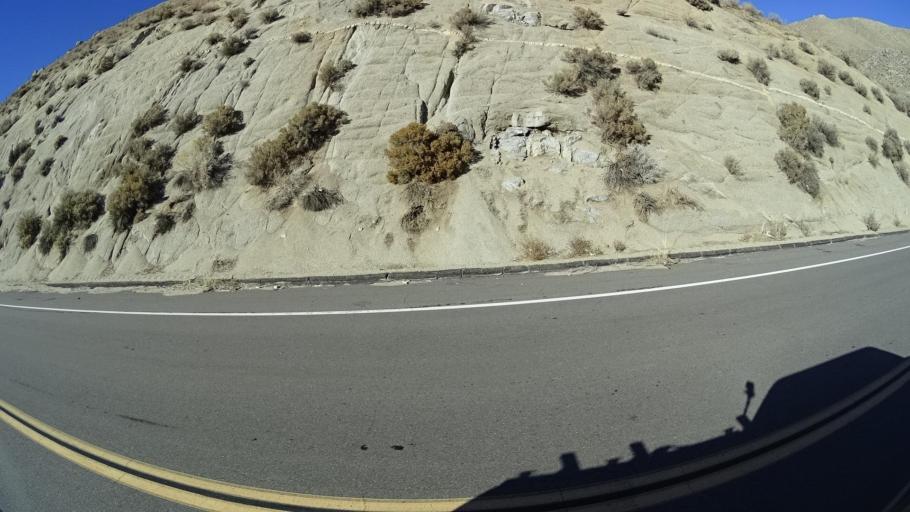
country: US
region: California
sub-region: Kern County
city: Weldon
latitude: 35.6728
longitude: -118.3464
